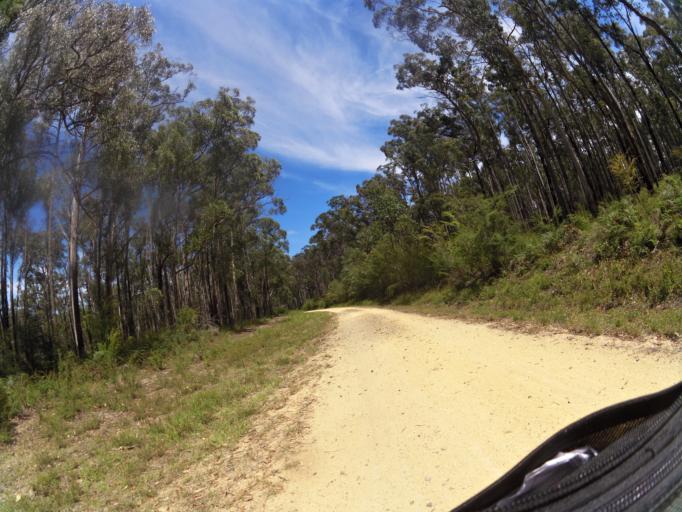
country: AU
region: Victoria
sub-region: East Gippsland
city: Lakes Entrance
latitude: -37.7313
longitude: 148.0829
